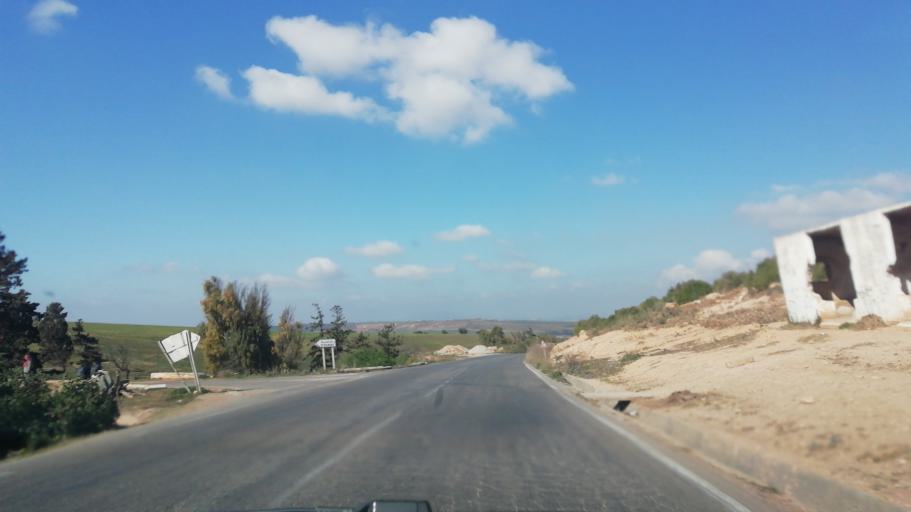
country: DZ
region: Oran
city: Ain el Bya
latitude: 35.7280
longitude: -0.2486
